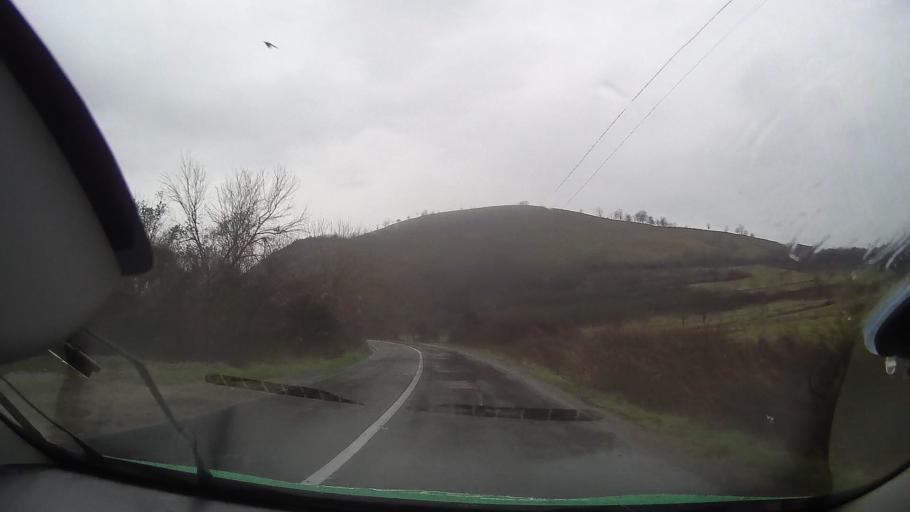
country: RO
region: Bihor
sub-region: Comuna Pocola
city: Pocola
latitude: 46.6866
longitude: 22.2609
